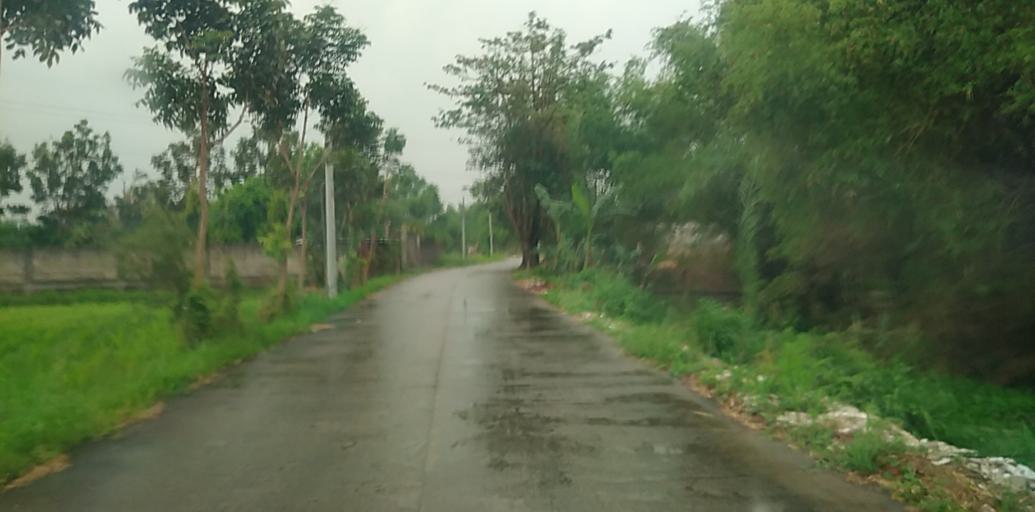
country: PH
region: Central Luzon
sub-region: Province of Pampanga
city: San Antonio
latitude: 15.1523
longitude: 120.6835
